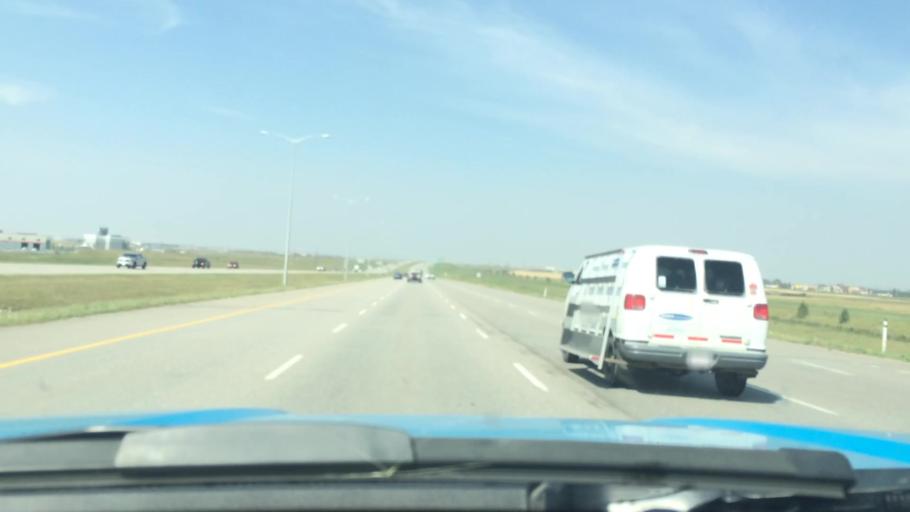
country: CA
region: Alberta
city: Chestermere
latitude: 50.9555
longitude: -113.9205
